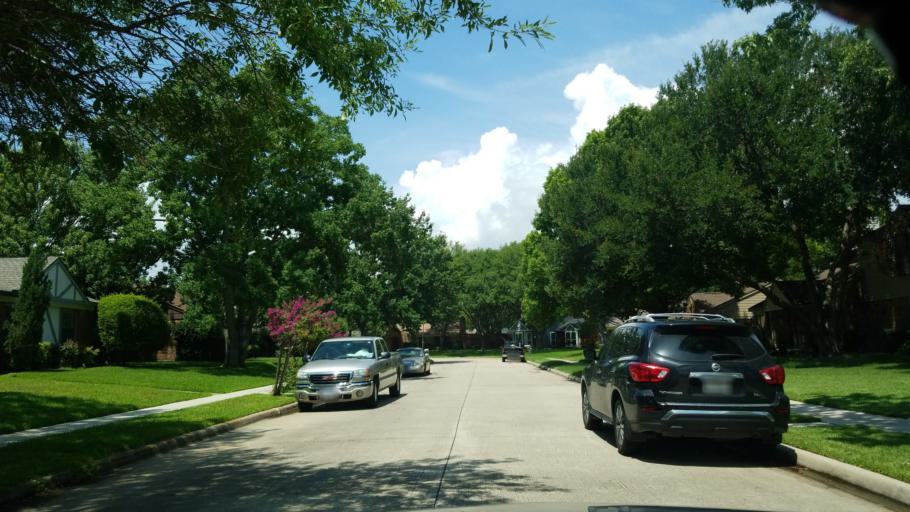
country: US
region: Texas
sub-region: Dallas County
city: Coppell
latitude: 32.9671
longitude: -96.9644
